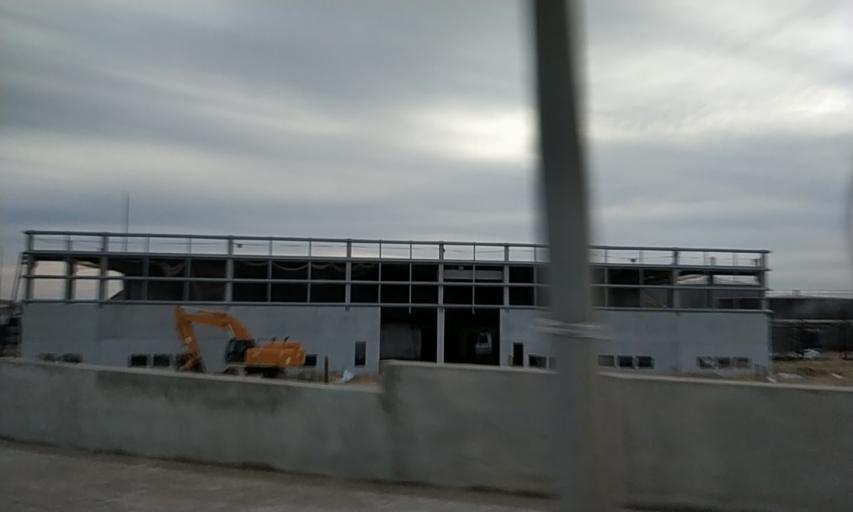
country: PT
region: Setubal
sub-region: Setubal
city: Setubal
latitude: 38.5000
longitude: -8.8366
